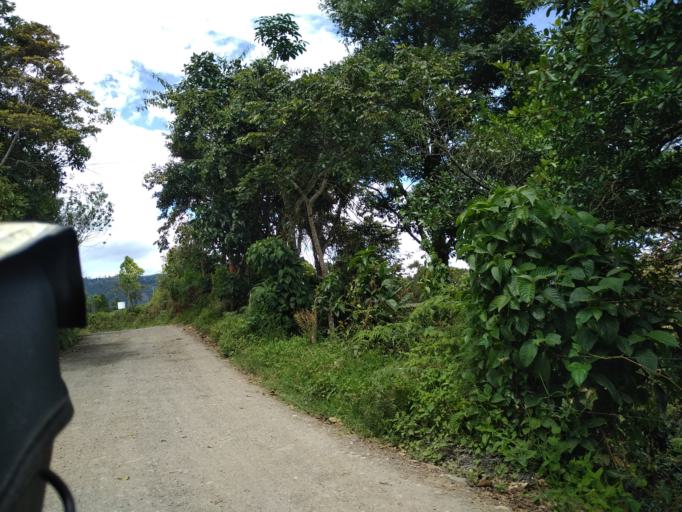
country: CO
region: Quindio
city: Salento
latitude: 4.6245
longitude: -75.5893
